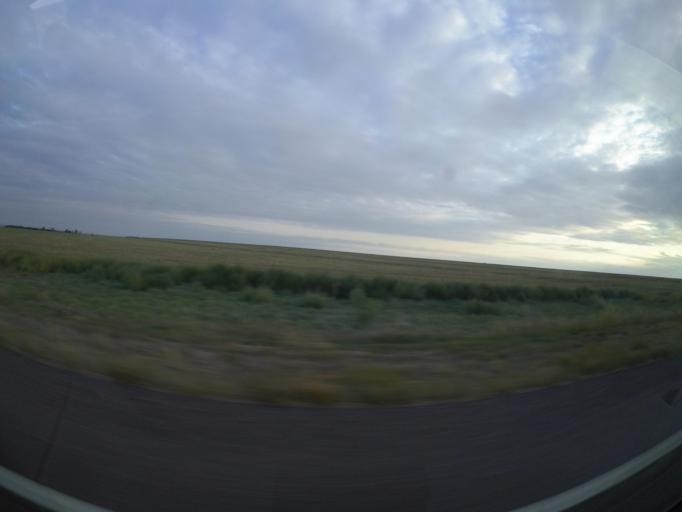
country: US
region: Kansas
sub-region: Cheyenne County
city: Saint Francis
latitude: 39.7459
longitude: -102.1345
